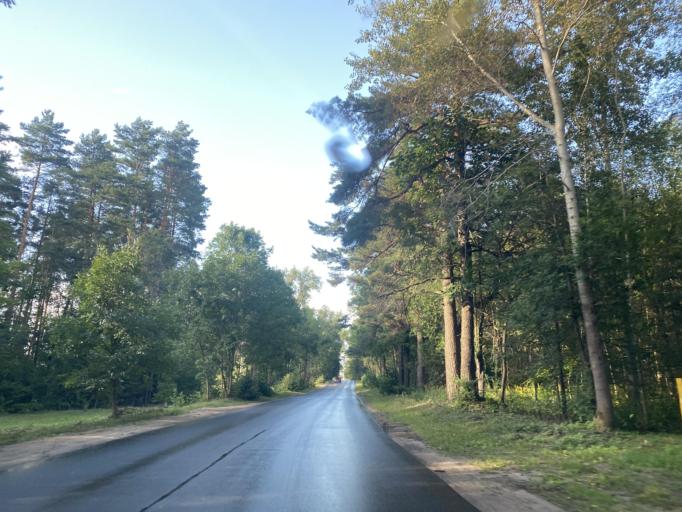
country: BY
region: Minsk
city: Borovlyany
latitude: 53.9229
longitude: 27.6537
